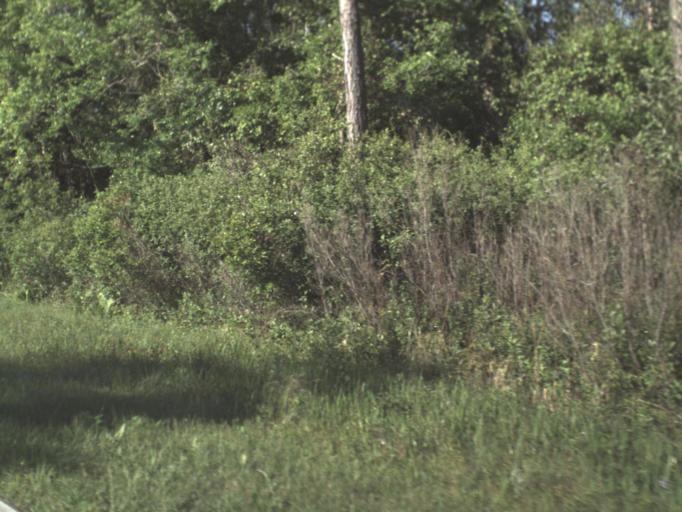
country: US
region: Florida
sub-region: Gulf County
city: Wewahitchka
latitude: 30.1088
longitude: -84.9868
